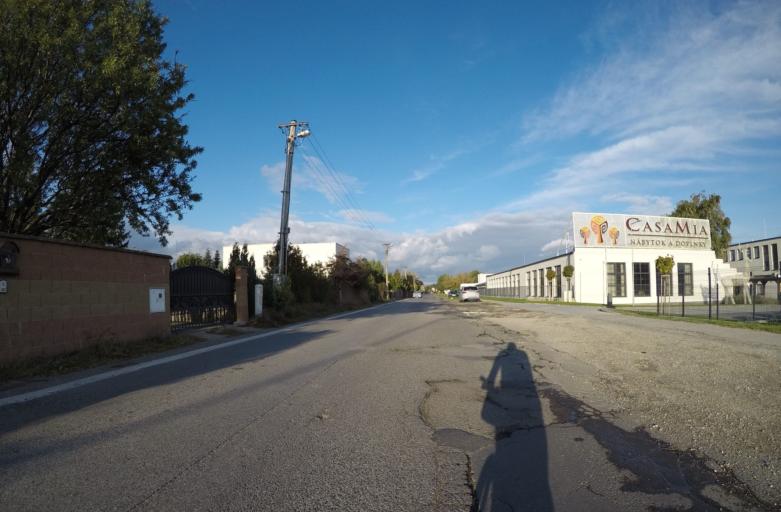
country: SK
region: Bratislavsky
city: Bratislava
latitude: 48.1754
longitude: 17.1706
